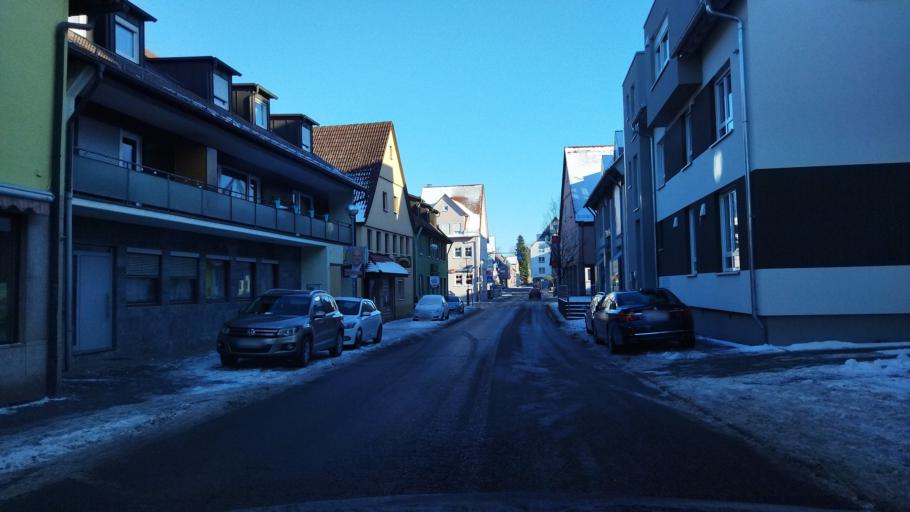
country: DE
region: Baden-Wuerttemberg
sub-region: Regierungsbezirk Stuttgart
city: Obersontheim
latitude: 49.0573
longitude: 9.8986
